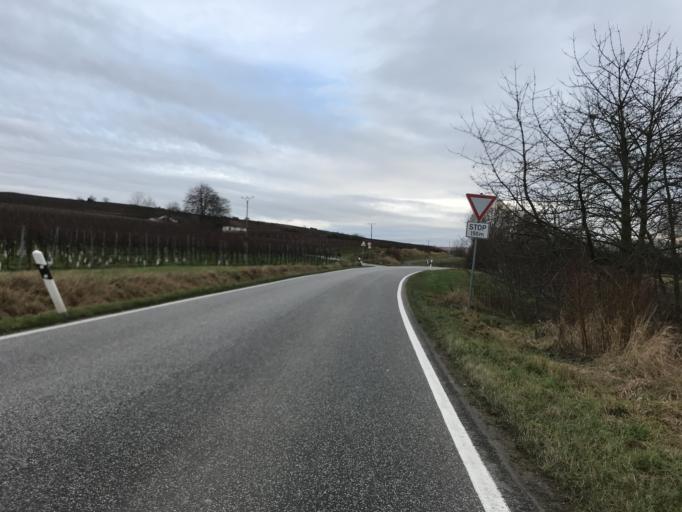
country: DE
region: Rheinland-Pfalz
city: Ingelheim am Rhein
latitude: 49.9562
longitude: 8.0700
